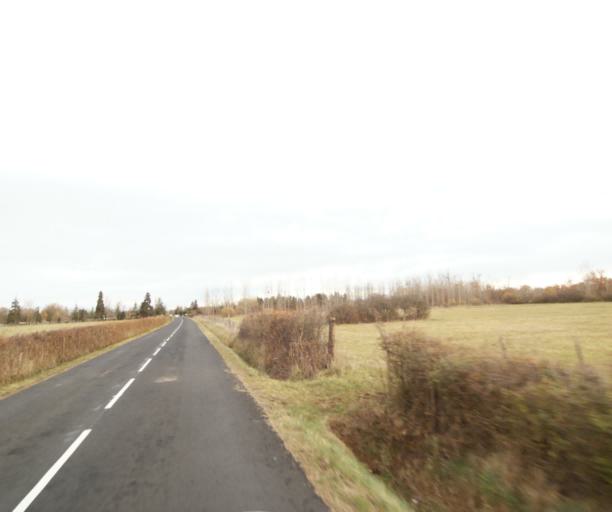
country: FR
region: Rhone-Alpes
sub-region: Departement de la Loire
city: Sury-le-Comtal
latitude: 45.5172
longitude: 4.1804
